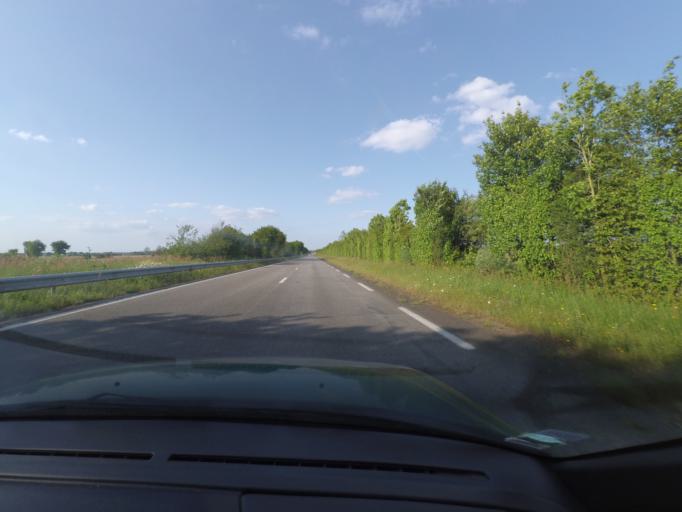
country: FR
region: Pays de la Loire
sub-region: Departement de la Vendee
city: Saligny
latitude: 46.8492
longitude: -1.4134
